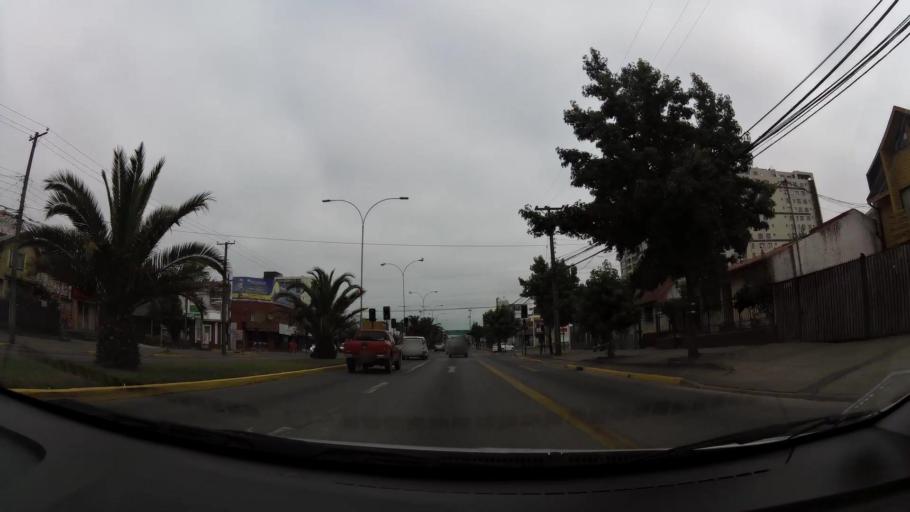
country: CL
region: Biobio
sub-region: Provincia de Concepcion
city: Concepcion
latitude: -36.8188
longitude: -73.0414
